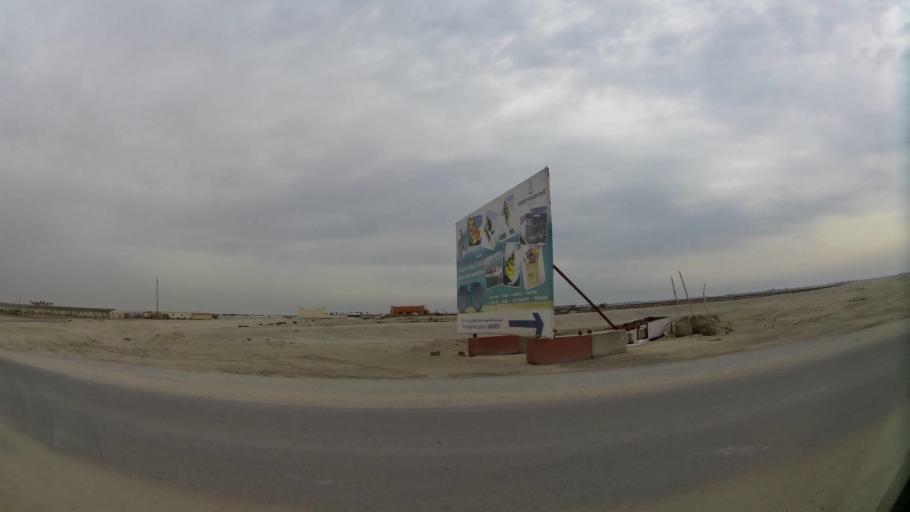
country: BH
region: Central Governorate
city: Dar Kulayb
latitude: 25.8390
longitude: 50.5874
